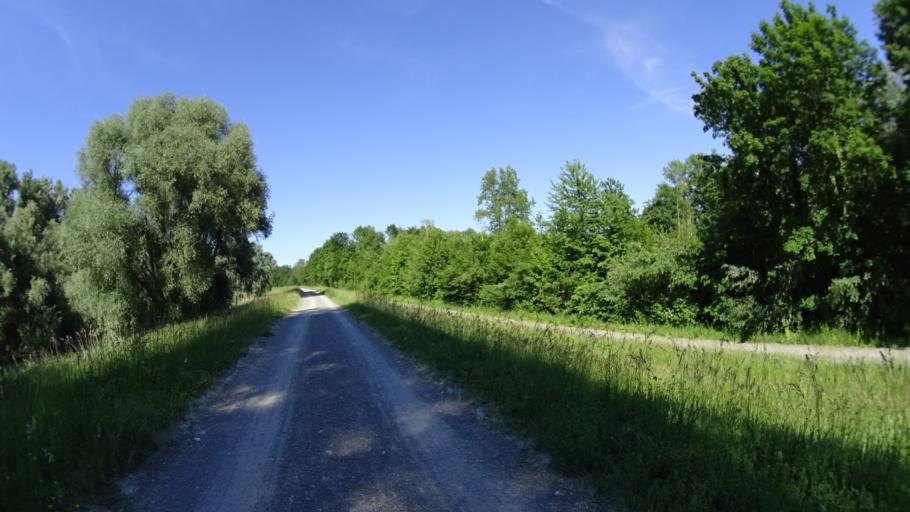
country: DE
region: Baden-Wuerttemberg
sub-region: Karlsruhe Region
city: Eggenstein-Leopoldshafen
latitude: 49.0881
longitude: 8.3621
